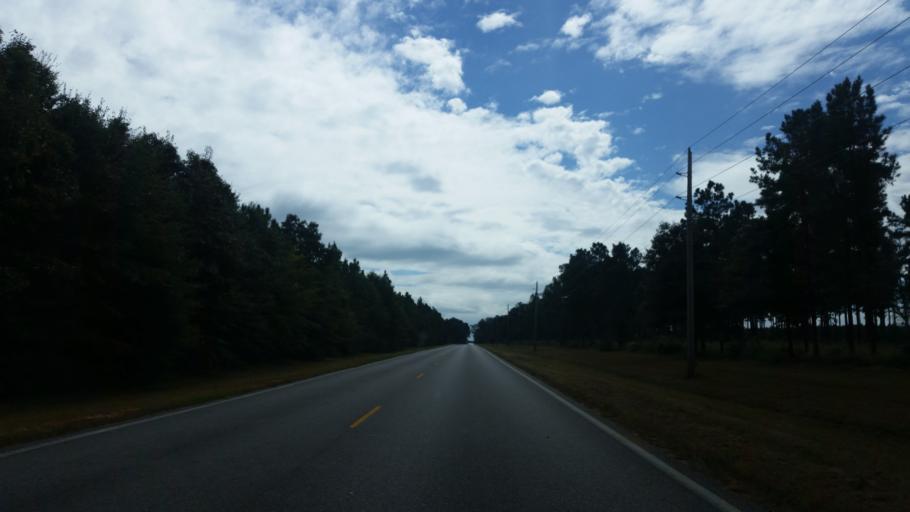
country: US
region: Florida
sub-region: Santa Rosa County
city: Point Baker
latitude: 30.7885
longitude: -86.9404
